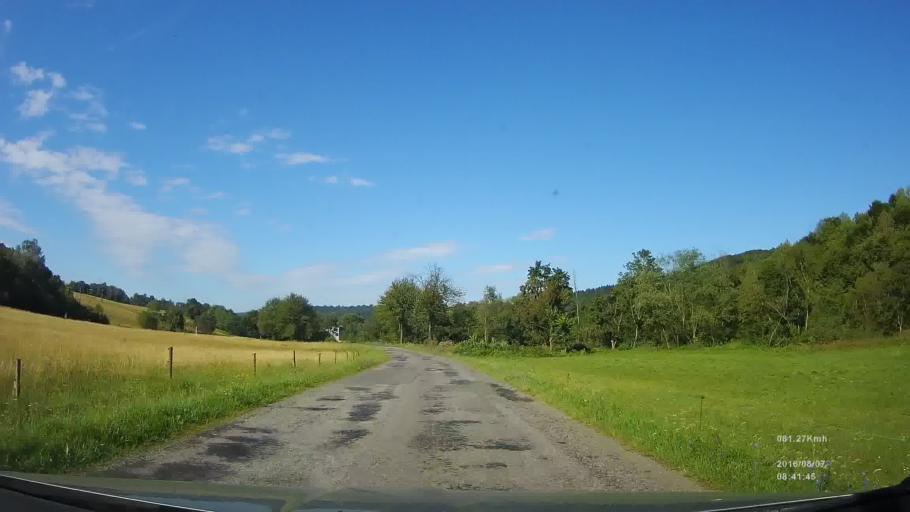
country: SK
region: Presovsky
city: Medzilaborce
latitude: 49.2881
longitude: 21.7675
